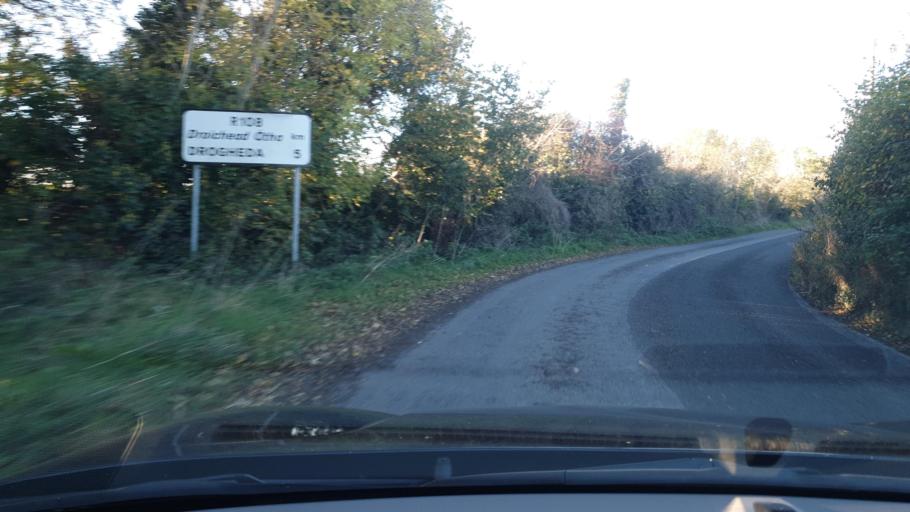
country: IE
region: Leinster
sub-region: Lu
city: Drogheda
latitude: 53.6726
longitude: -6.3252
